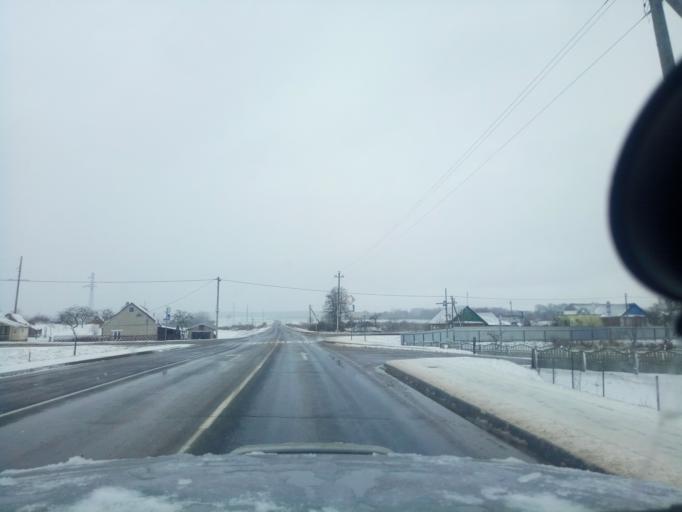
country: BY
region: Minsk
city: Nyasvizh
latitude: 53.2087
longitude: 26.6617
